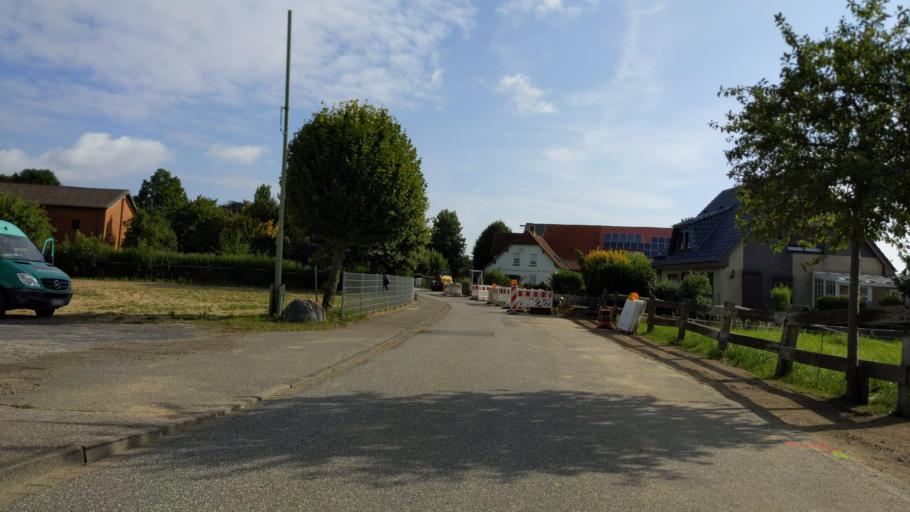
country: DE
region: Schleswig-Holstein
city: Bad Schwartau
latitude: 53.9896
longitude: 10.6641
